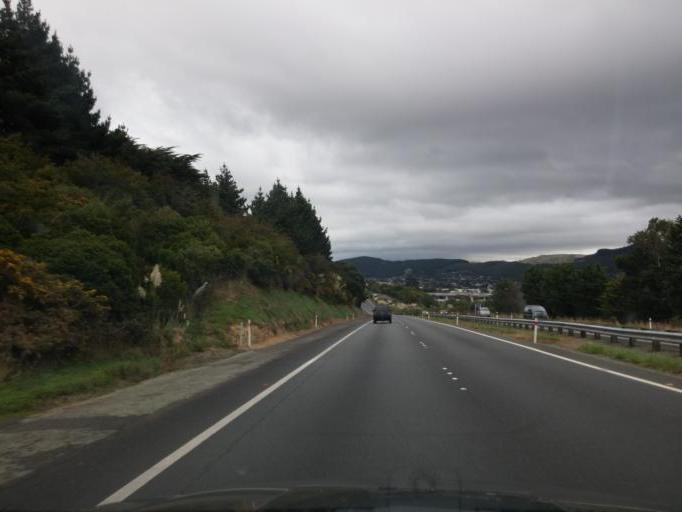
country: NZ
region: Wellington
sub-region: Porirua City
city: Porirua
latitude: -41.1565
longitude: 174.8387
